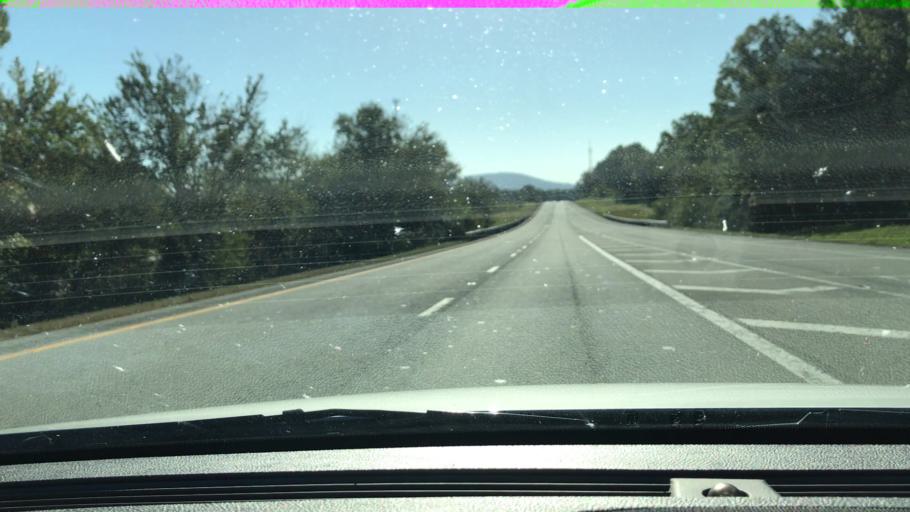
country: US
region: Tennessee
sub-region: Cumberland County
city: Fairfield Glade
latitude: 35.9478
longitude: -84.9424
